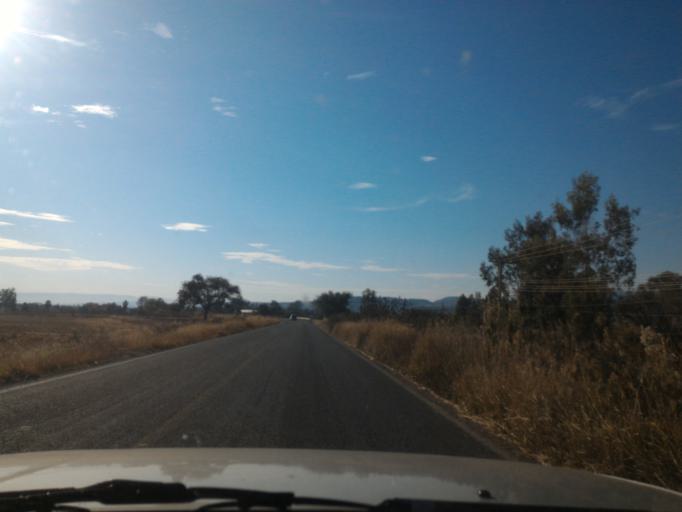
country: MX
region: Guanajuato
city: Ciudad Manuel Doblado
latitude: 20.7893
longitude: -101.9830
